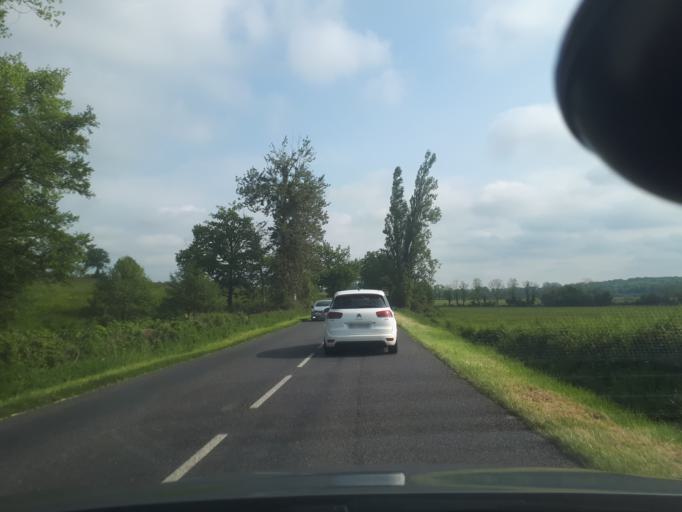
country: FR
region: Auvergne
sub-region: Departement de l'Allier
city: Saint-Gerand-le-Puy
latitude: 46.3640
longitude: 3.5788
